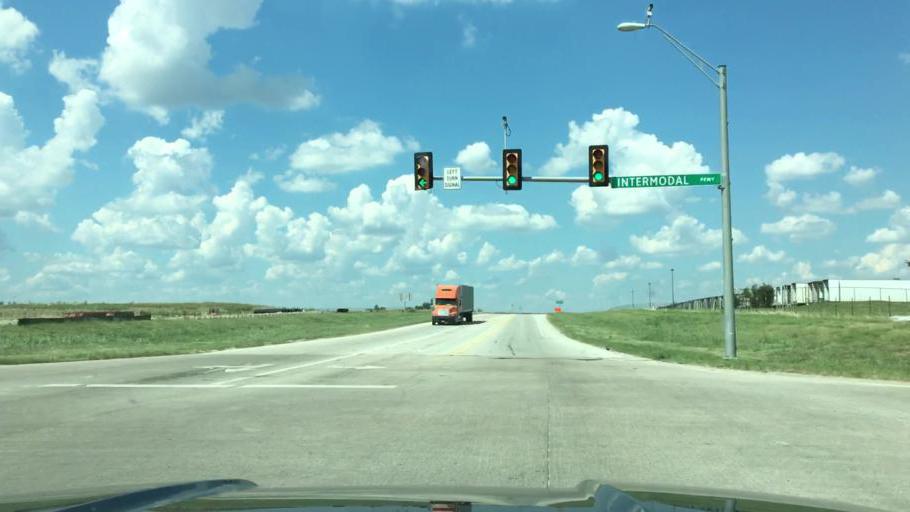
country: US
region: Texas
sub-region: Tarrant County
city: Haslet
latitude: 32.9899
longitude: -97.3423
